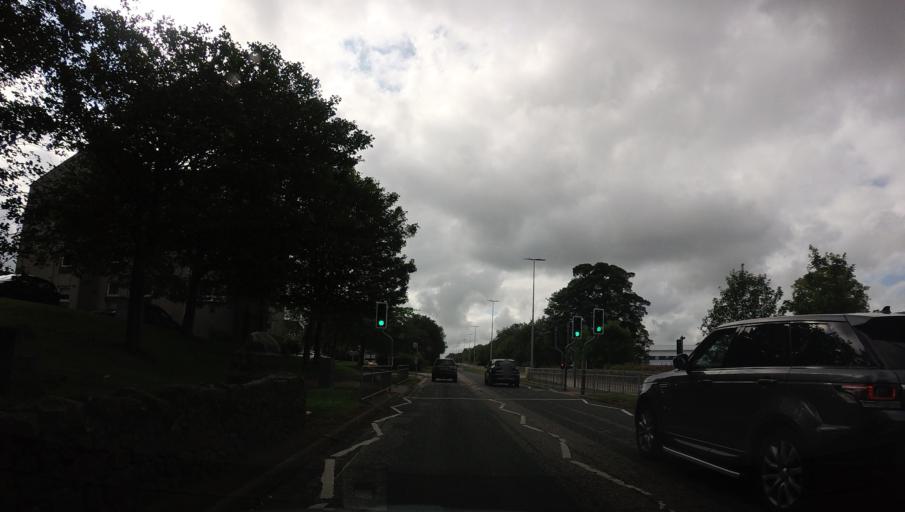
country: GB
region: Scotland
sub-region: Aberdeen City
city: Cults
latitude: 57.1522
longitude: -2.1419
